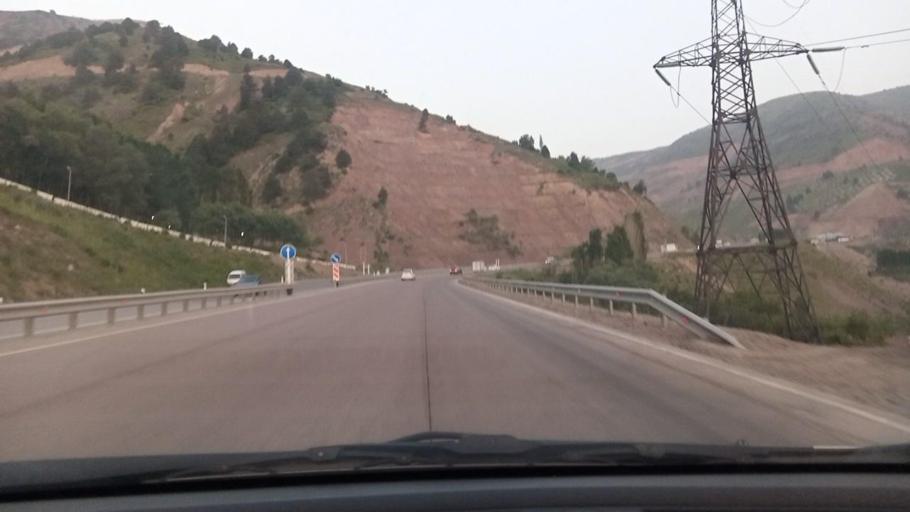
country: UZ
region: Toshkent
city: Angren
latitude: 41.1159
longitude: 70.4955
